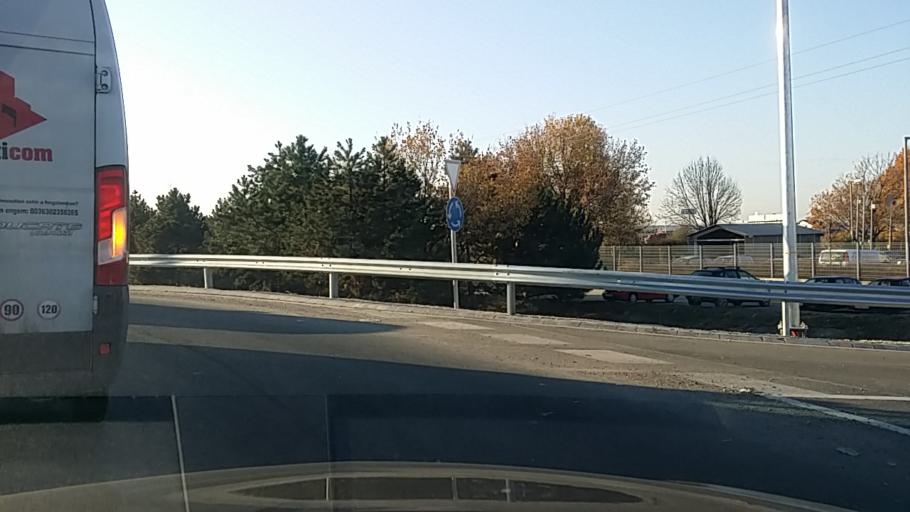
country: HU
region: Pest
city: Szigetszentmiklos
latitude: 47.3814
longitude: 19.0494
